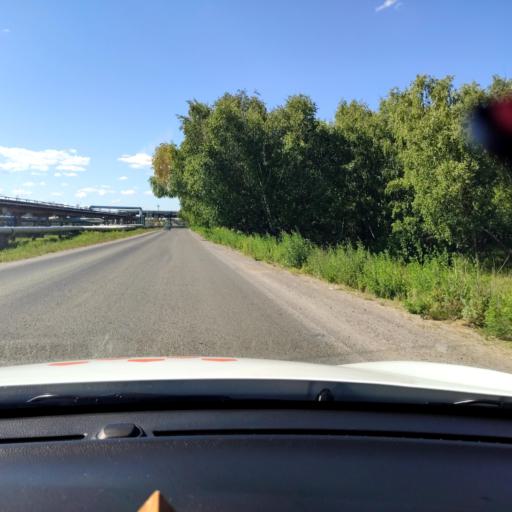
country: RU
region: Tatarstan
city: Staroye Arakchino
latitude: 55.8674
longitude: 48.9726
